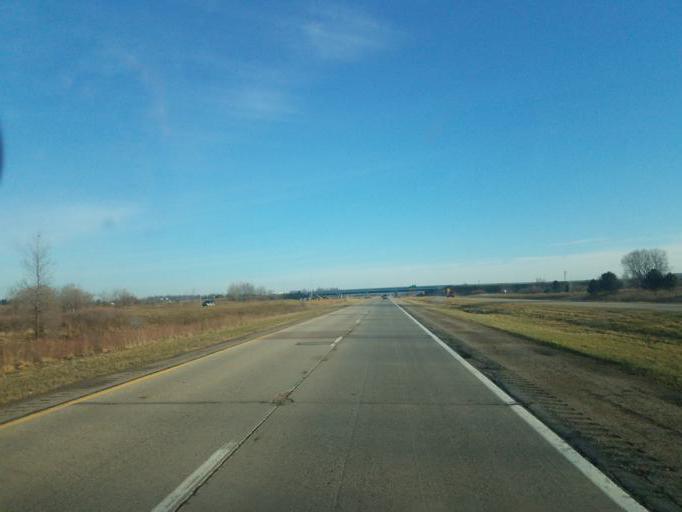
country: US
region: Michigan
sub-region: Clinton County
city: Bath
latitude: 42.8013
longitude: -84.5116
